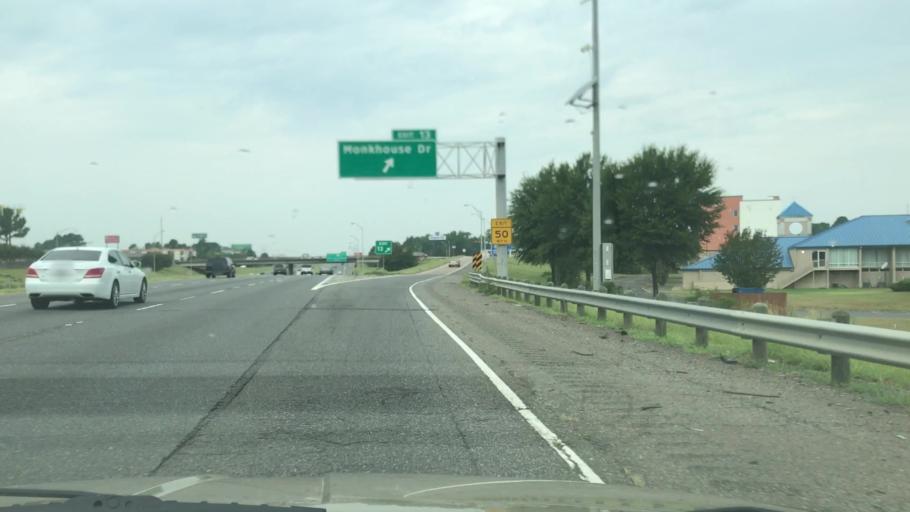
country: US
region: Louisiana
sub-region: Caddo Parish
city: Shreveport
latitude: 32.4629
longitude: -93.8242
